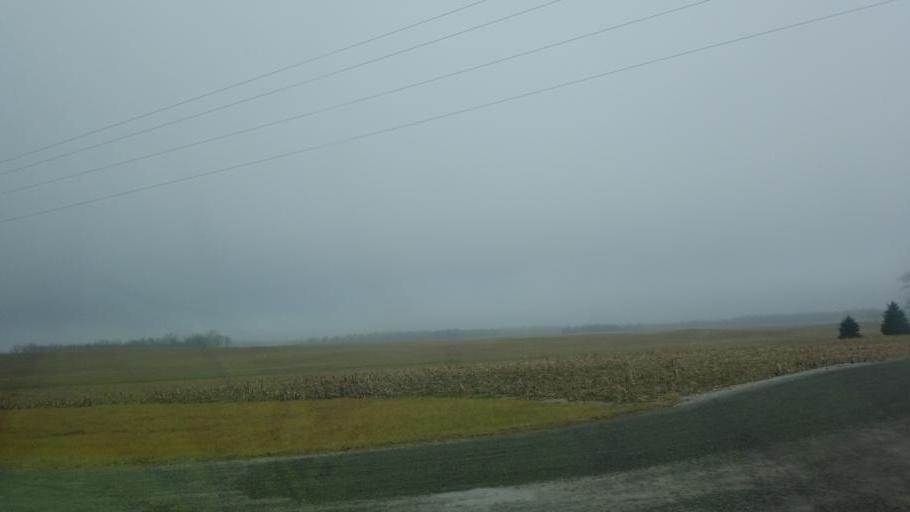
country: US
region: Ohio
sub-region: Champaign County
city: North Lewisburg
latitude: 40.2576
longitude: -83.5834
